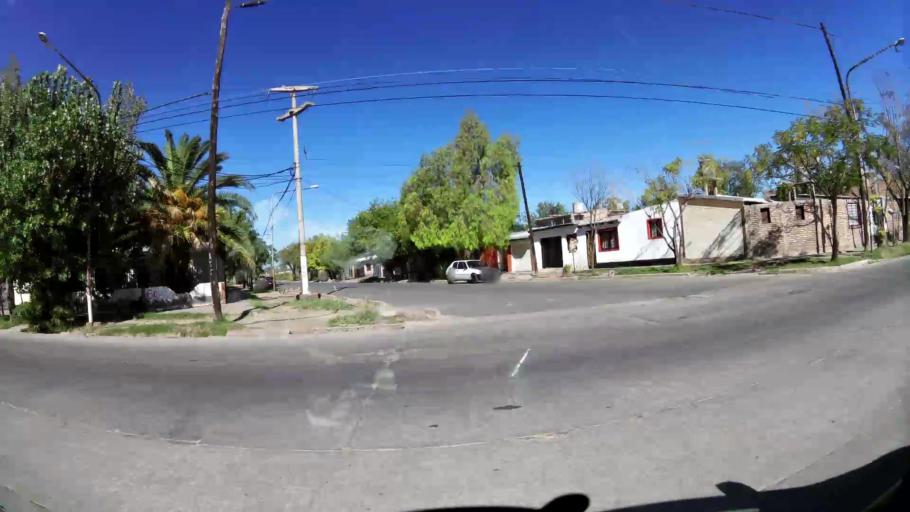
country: AR
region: Mendoza
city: Las Heras
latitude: -32.8393
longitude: -68.8183
